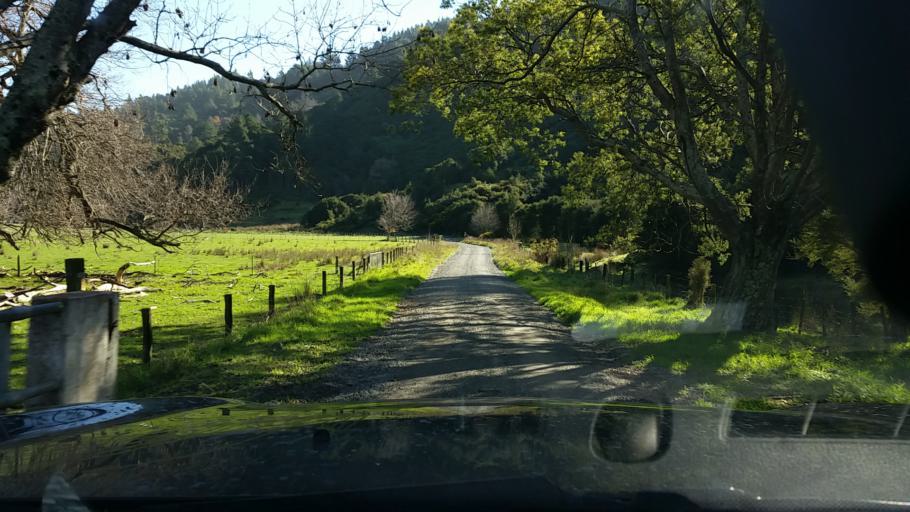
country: NZ
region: Marlborough
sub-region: Marlborough District
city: Blenheim
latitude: -41.4597
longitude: 173.7863
